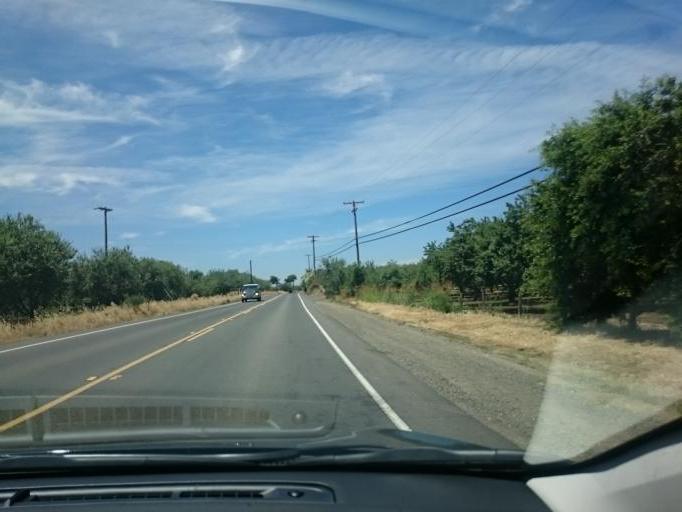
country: US
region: California
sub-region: Stanislaus County
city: Waterford
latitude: 37.6447
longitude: -120.7030
